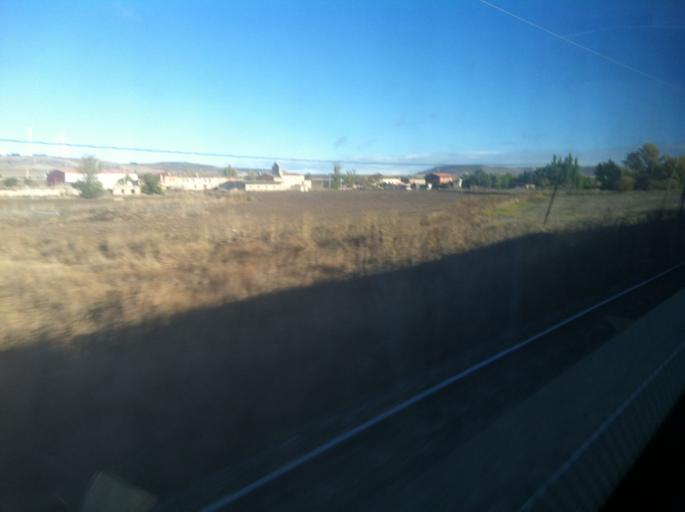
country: ES
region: Castille and Leon
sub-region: Provincia de Burgos
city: Villaquiran de los Infantes
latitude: 42.2222
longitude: -3.9926
